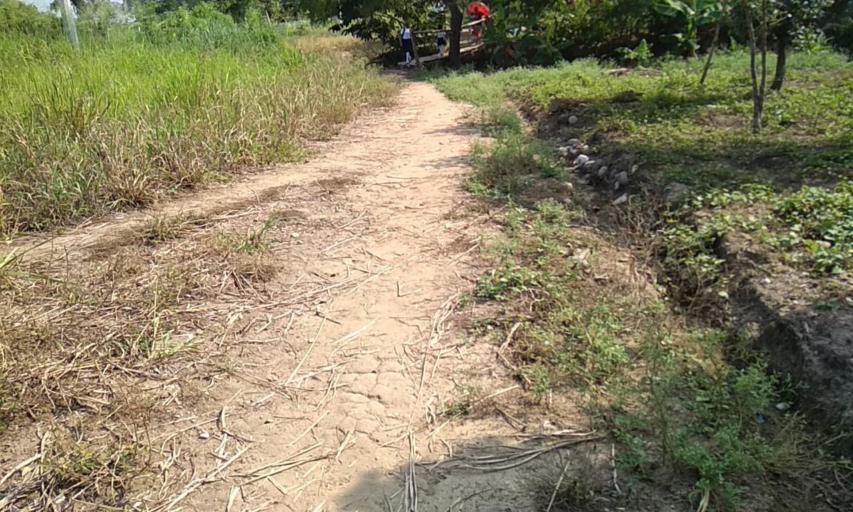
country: MX
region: Veracruz
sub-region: Atzalan
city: Colonias Pedernales
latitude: 20.0510
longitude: -96.9916
